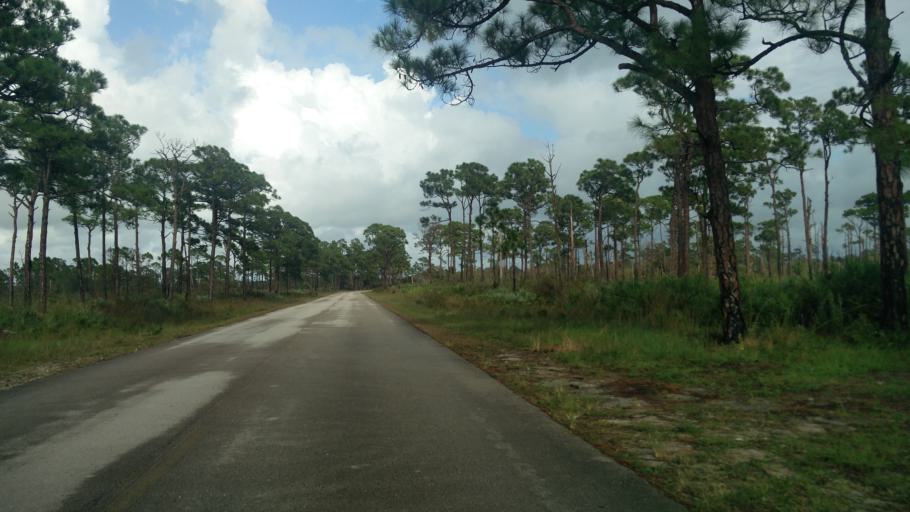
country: US
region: Florida
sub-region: Palm Beach County
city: Tequesta
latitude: 27.0097
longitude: -80.1242
